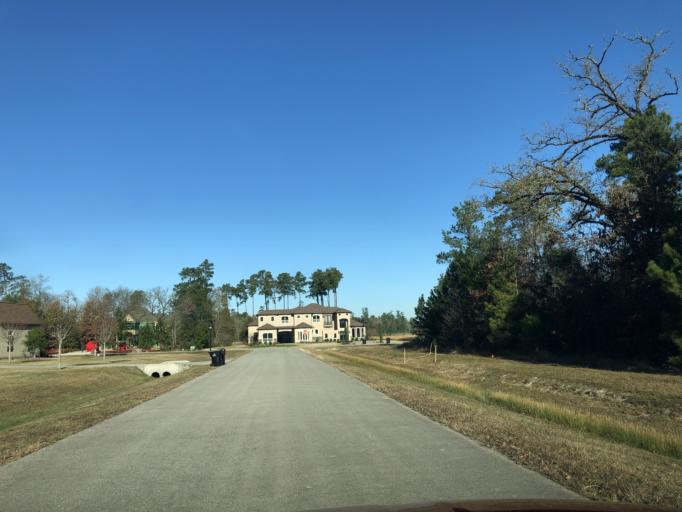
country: US
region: Texas
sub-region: Montgomery County
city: Porter Heights
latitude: 30.0703
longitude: -95.3189
